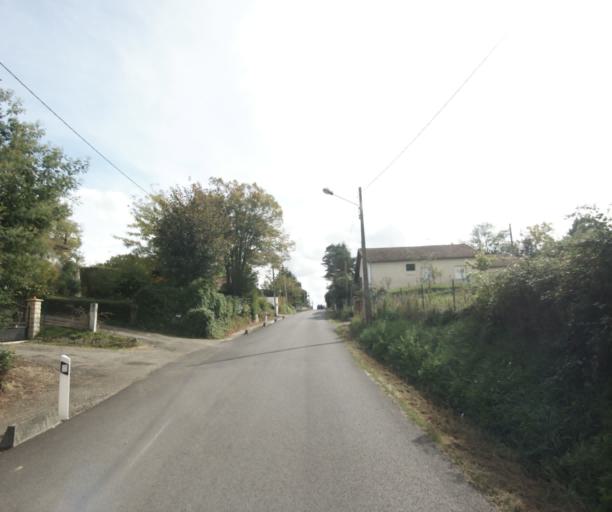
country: FR
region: Midi-Pyrenees
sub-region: Departement du Gers
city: Eauze
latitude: 43.8531
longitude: 0.1034
